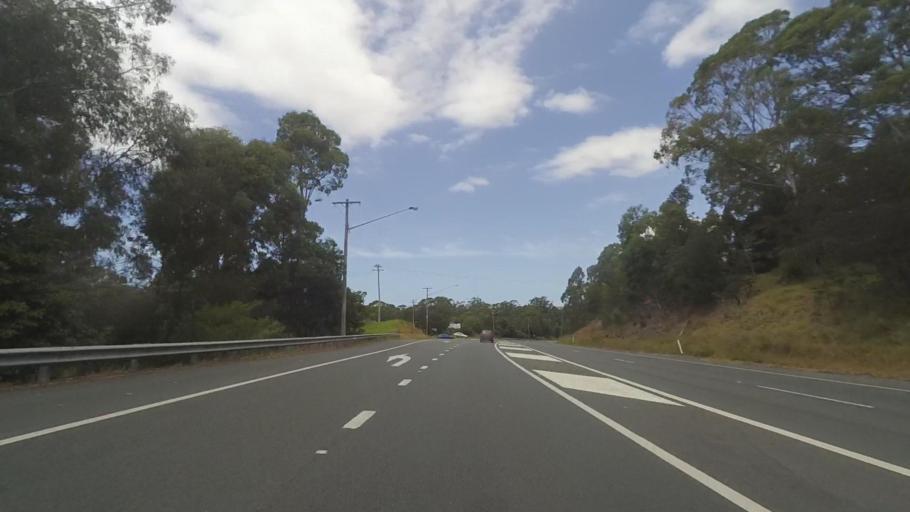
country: AU
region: New South Wales
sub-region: Shoalhaven Shire
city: Milton
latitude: -35.2582
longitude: 150.4275
